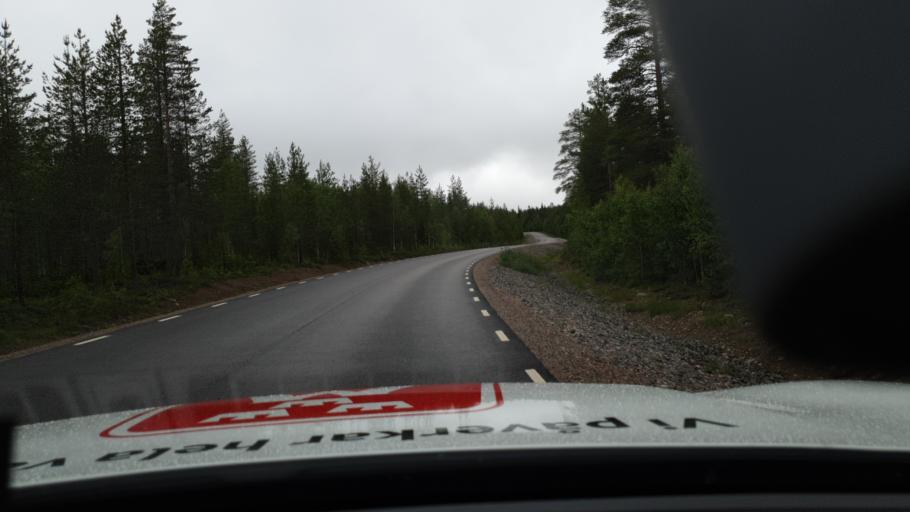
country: SE
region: Norrbotten
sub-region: Overtornea Kommun
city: OEvertornea
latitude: 66.4338
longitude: 23.5141
